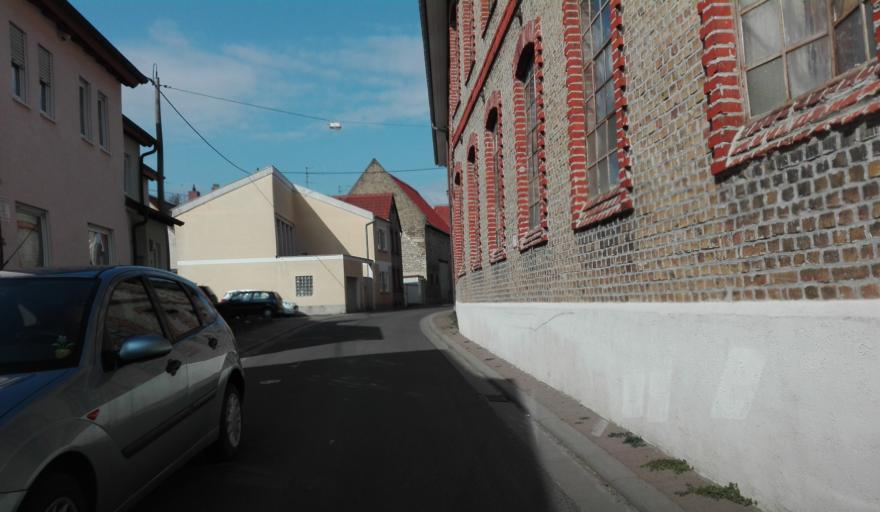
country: DE
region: Rheinland-Pfalz
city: Bermersheim
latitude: 49.6636
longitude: 8.2089
